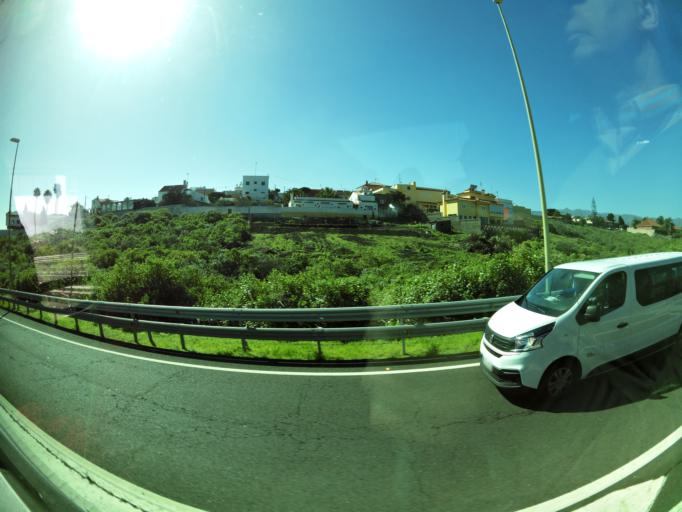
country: ES
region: Canary Islands
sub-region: Provincia de Las Palmas
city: Santa Brigida
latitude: 28.0508
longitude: -15.4578
